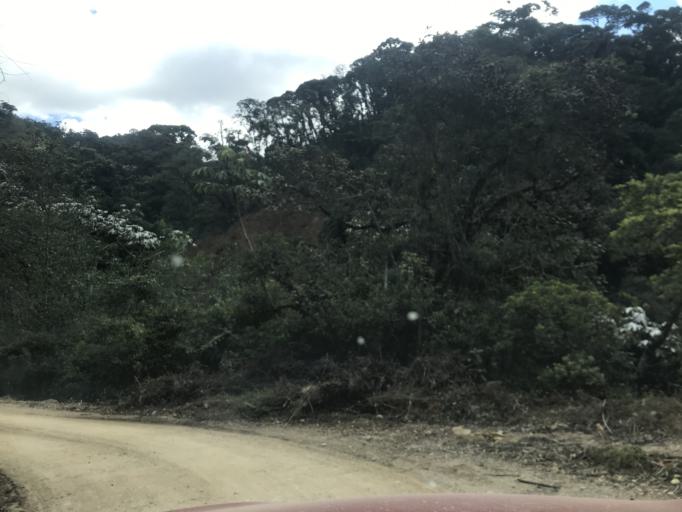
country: PE
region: Cajamarca
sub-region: Provincia de Chota
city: Querocoto
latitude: -6.3501
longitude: -79.0586
